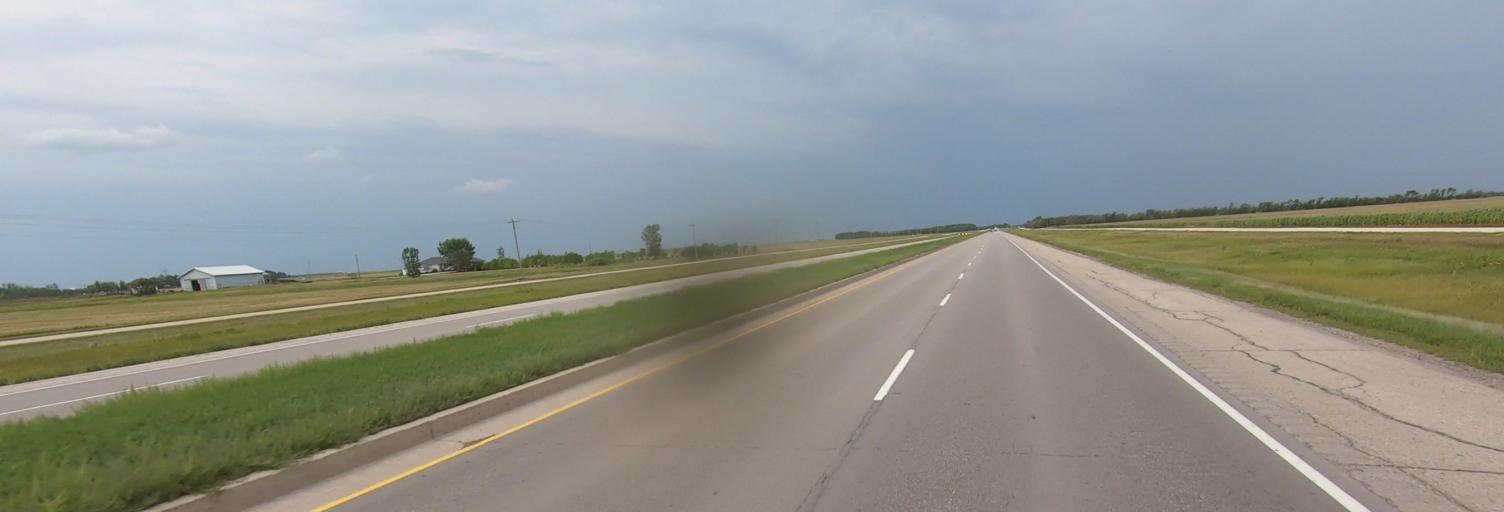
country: CA
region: Manitoba
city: Winnipeg
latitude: 49.7680
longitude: -97.2665
